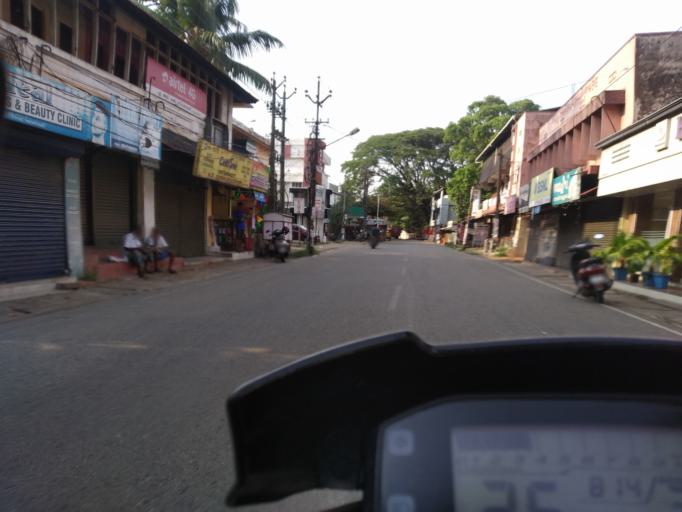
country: IN
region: Kerala
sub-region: Alappuzha
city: Arukutti
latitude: 9.9491
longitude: 76.3472
